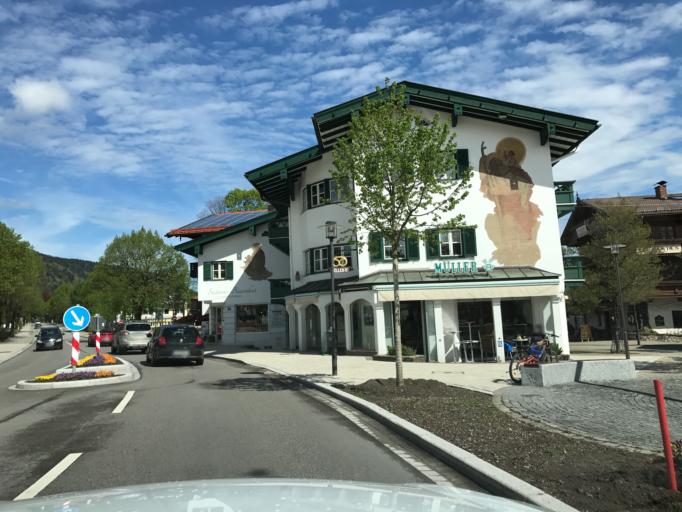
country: DE
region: Bavaria
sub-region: Upper Bavaria
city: Bad Wiessee
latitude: 47.7127
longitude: 11.7255
